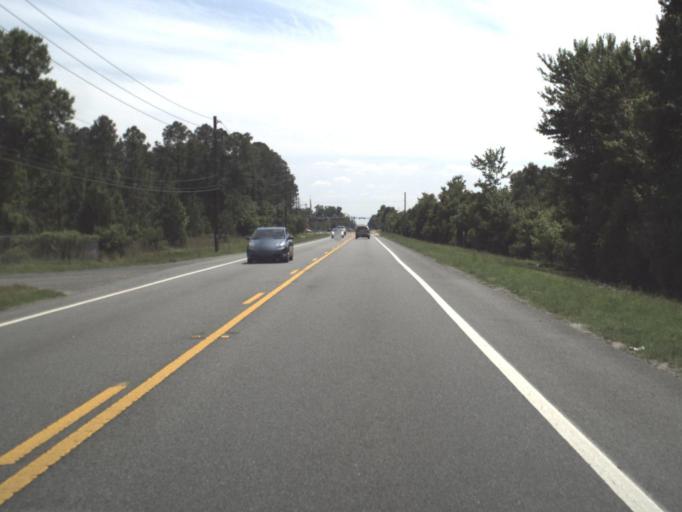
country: US
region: Florida
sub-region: Duval County
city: Jacksonville
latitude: 30.4796
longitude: -81.6286
